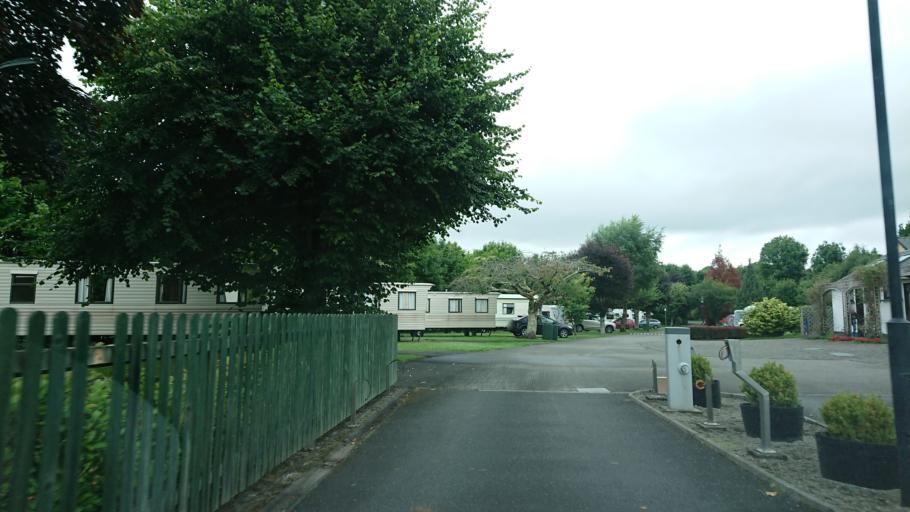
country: IE
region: Munster
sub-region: Ciarrai
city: Cill Airne
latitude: 52.0560
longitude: -9.4743
